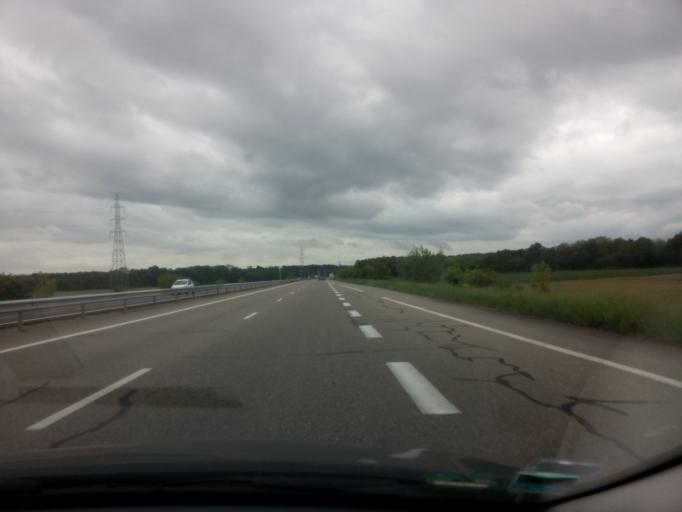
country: FR
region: Alsace
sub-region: Departement du Bas-Rhin
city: Soufflenheim
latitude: 48.7969
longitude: 7.9702
